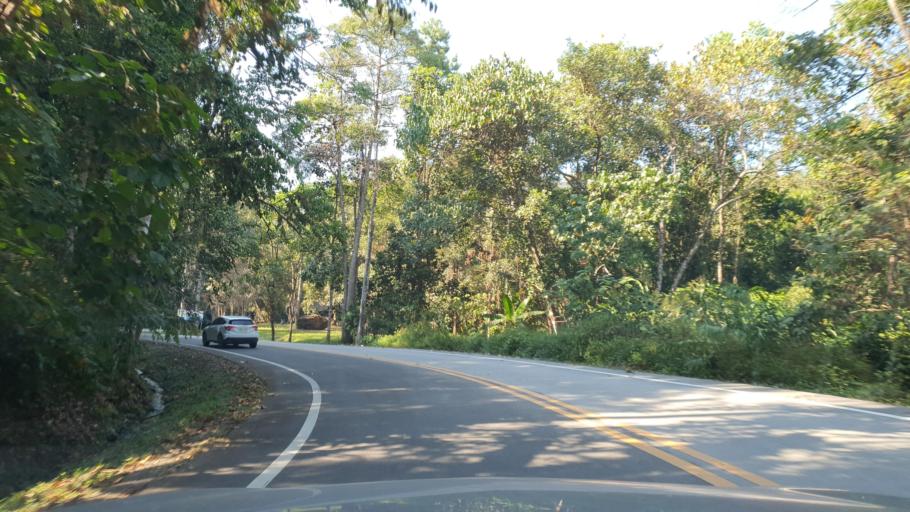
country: TH
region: Chiang Rai
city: Mae Lao
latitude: 19.8745
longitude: 99.6276
